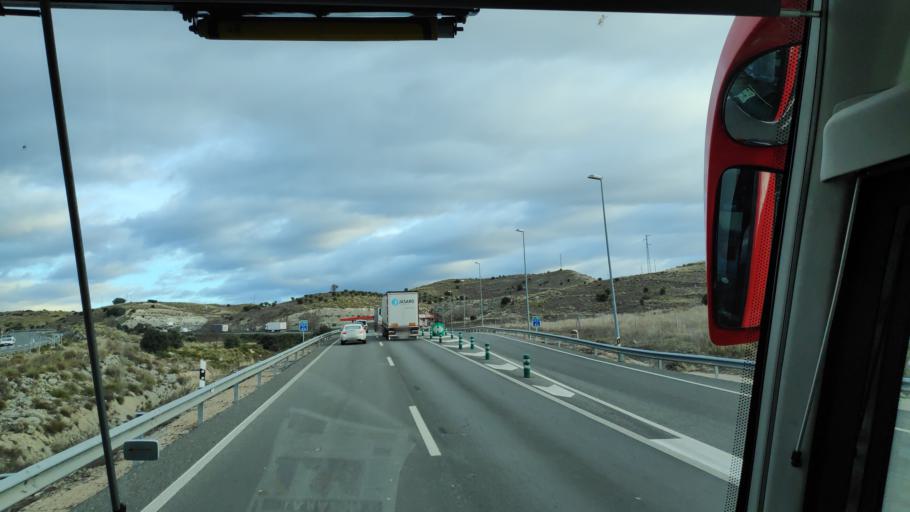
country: ES
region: Madrid
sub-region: Provincia de Madrid
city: Perales de Tajuna
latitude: 40.2092
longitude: -3.3219
